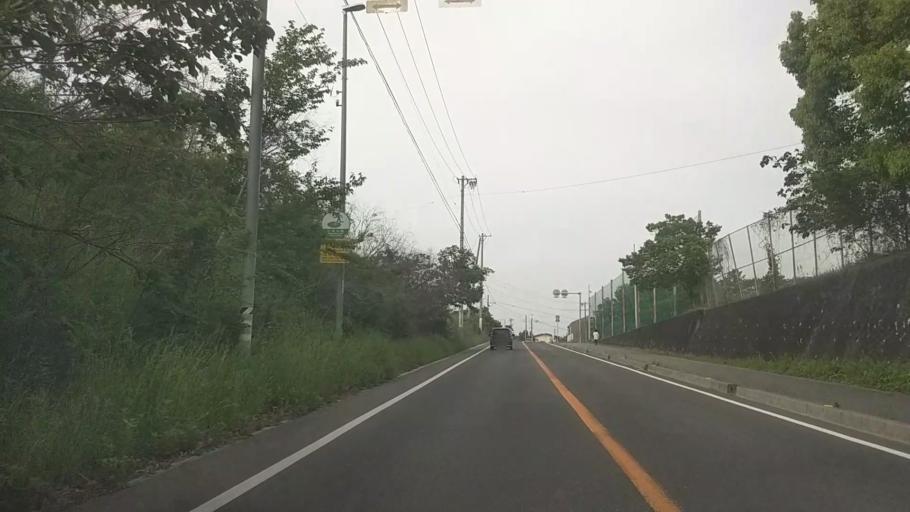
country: JP
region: Shizuoka
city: Hamamatsu
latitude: 34.7553
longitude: 137.6552
